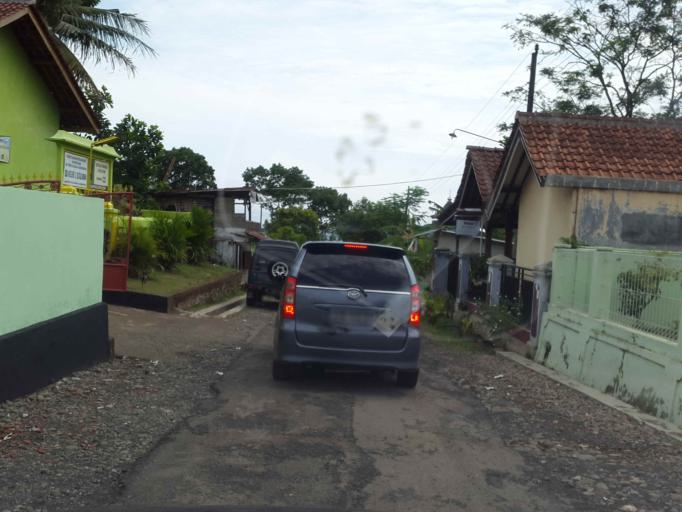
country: ID
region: Central Java
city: Baturaden
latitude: -7.3577
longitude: 109.2171
